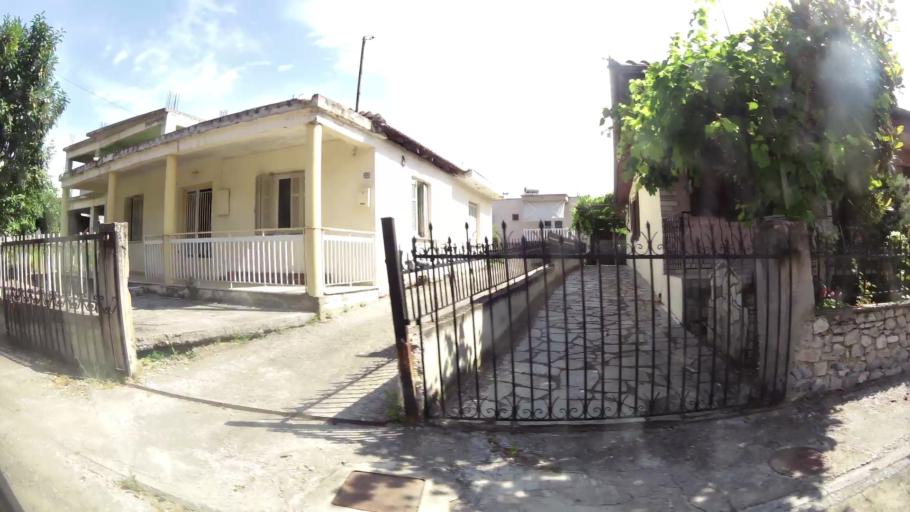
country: GR
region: Central Macedonia
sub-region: Nomos Pierias
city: Katerini
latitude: 40.2741
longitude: 22.4894
